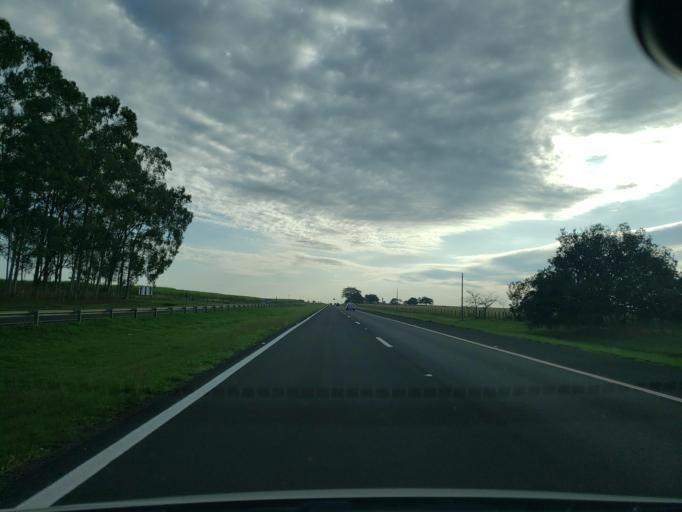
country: BR
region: Sao Paulo
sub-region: Guararapes
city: Guararapes
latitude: -21.2135
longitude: -50.7047
